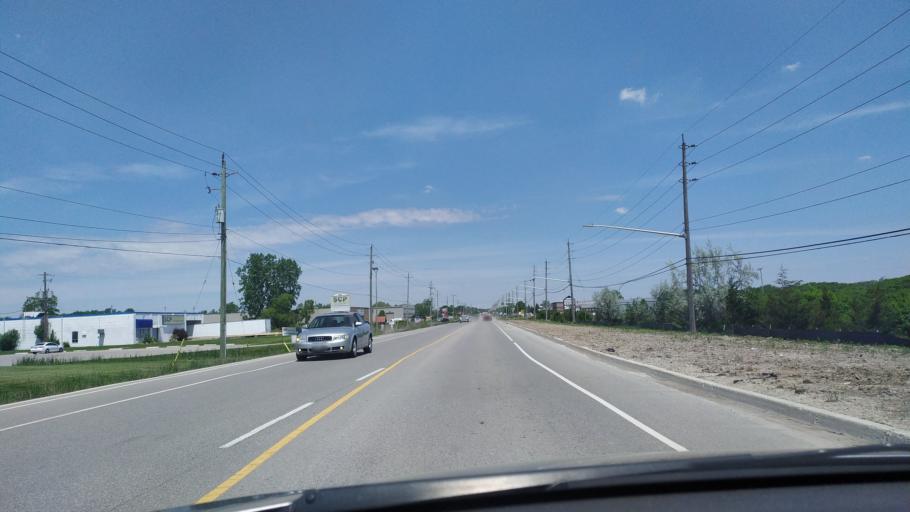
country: CA
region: Ontario
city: London
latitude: 42.9244
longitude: -81.2481
